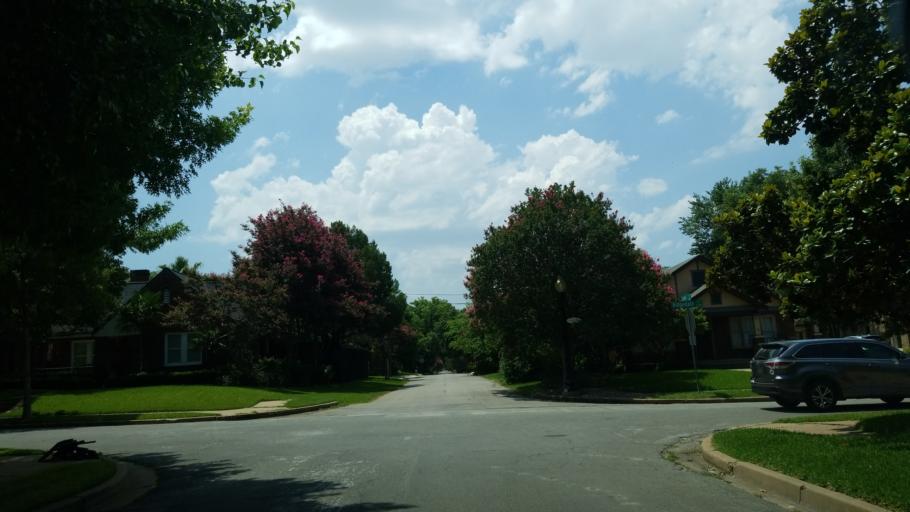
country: US
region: Texas
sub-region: Dallas County
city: Highland Park
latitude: 32.8257
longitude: -96.7799
